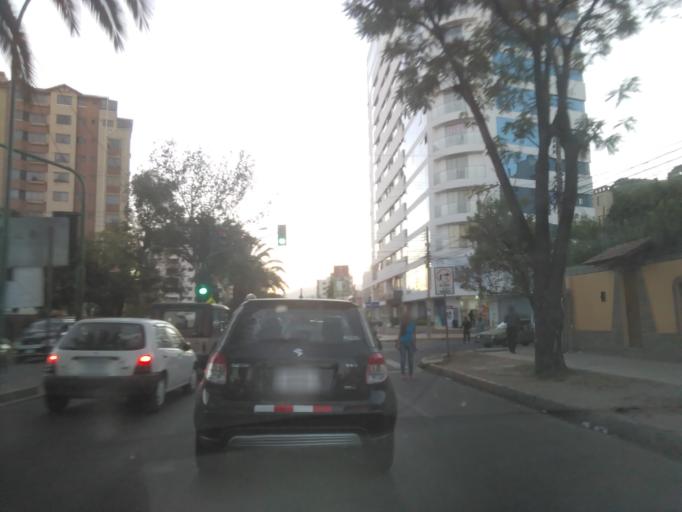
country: BO
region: Cochabamba
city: Cochabamba
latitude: -17.3724
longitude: -66.1635
